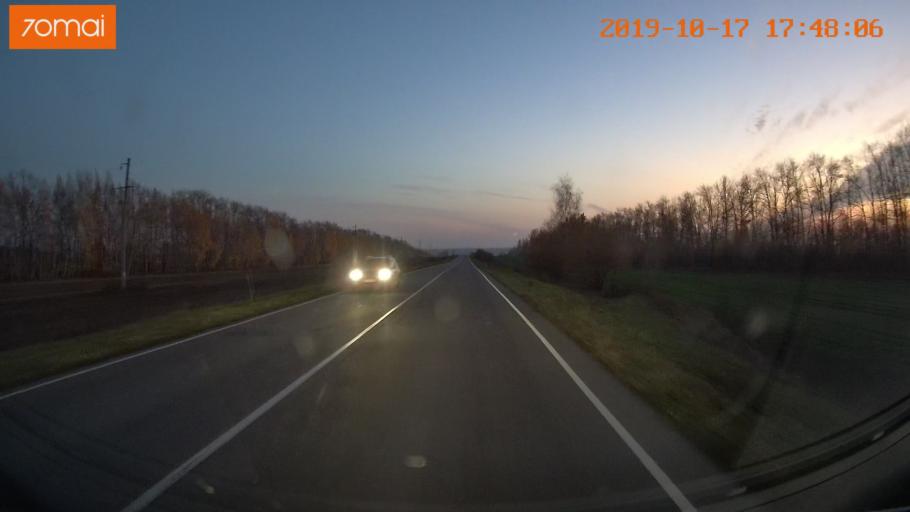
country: RU
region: Tula
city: Yepifan'
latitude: 53.6973
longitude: 38.6964
